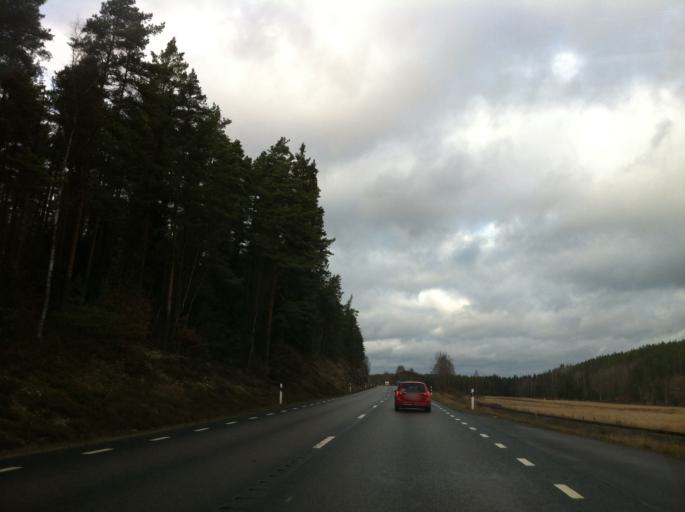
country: SE
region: Kalmar
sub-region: Hultsfreds Kommun
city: Hultsfred
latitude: 57.5346
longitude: 15.8138
